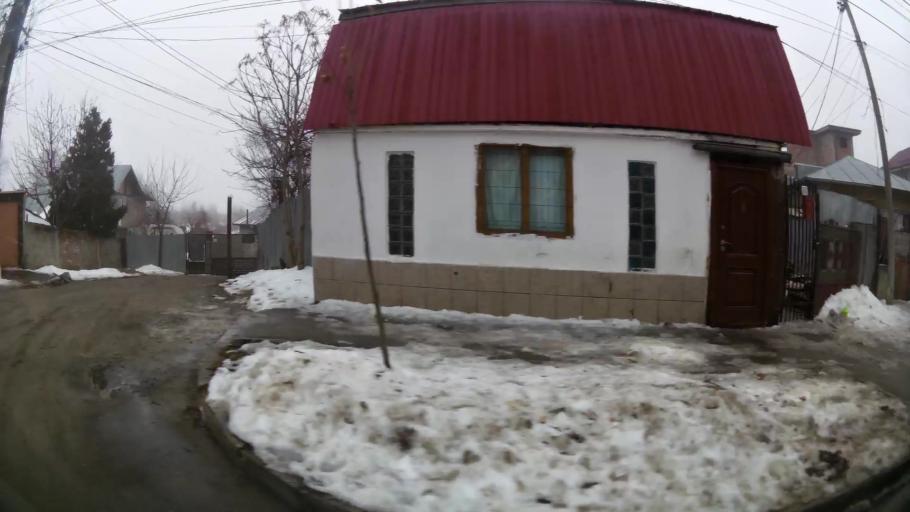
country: RO
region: Ilfov
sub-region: Comuna Chiajna
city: Rosu
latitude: 44.4703
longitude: 26.0019
